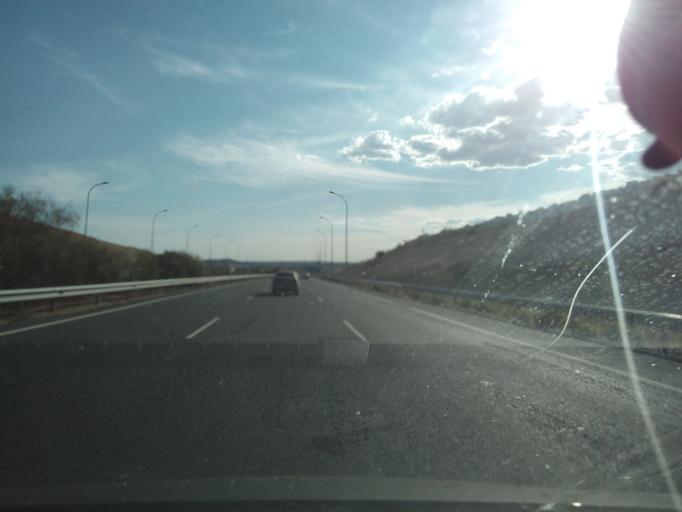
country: ES
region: Madrid
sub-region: Provincia de Madrid
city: Villa de Vallecas
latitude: 40.3412
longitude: -3.6002
